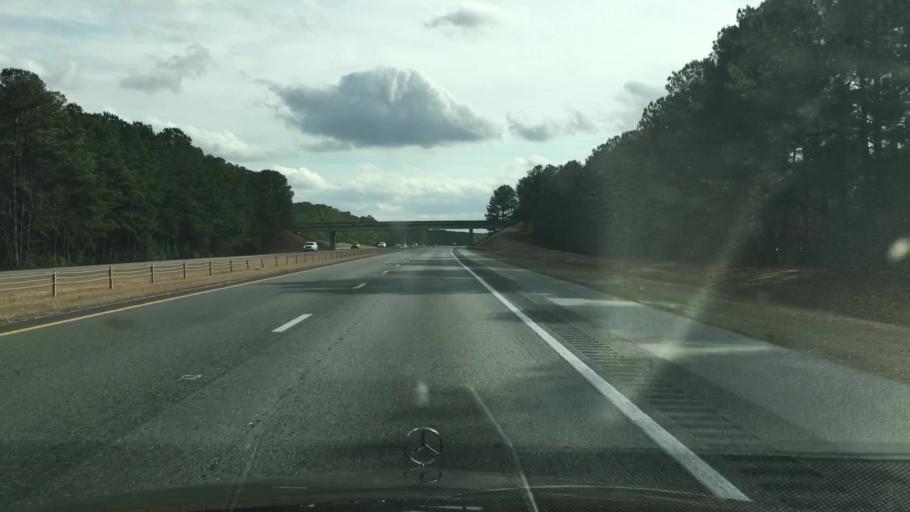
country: US
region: North Carolina
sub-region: Duplin County
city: Warsaw
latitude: 35.0517
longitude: -78.1555
